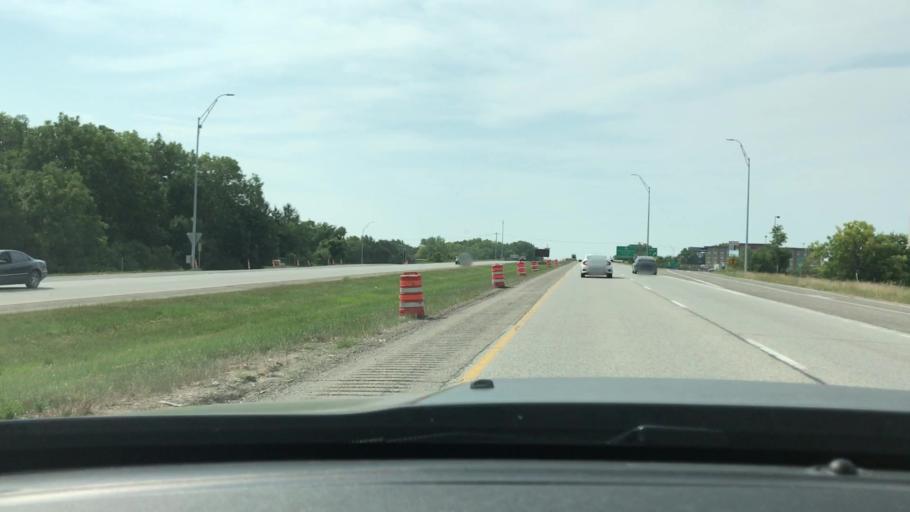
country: US
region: Iowa
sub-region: Scott County
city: Bettendorf
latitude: 41.5440
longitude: -90.5187
